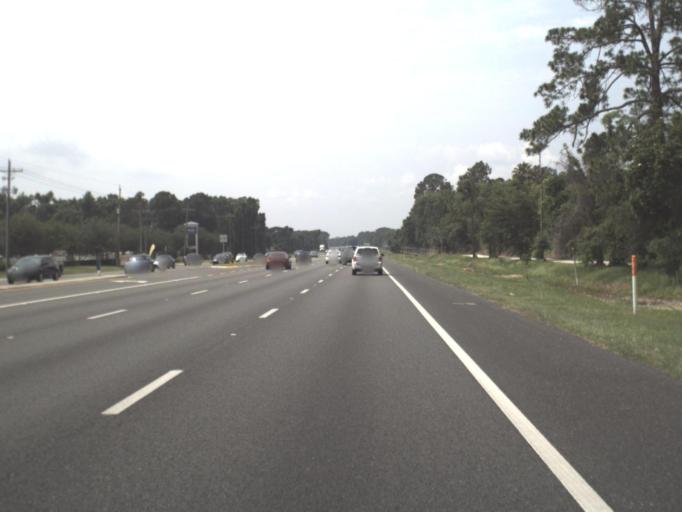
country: US
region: Florida
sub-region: Clay County
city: Orange Park
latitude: 30.1349
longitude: -81.7025
